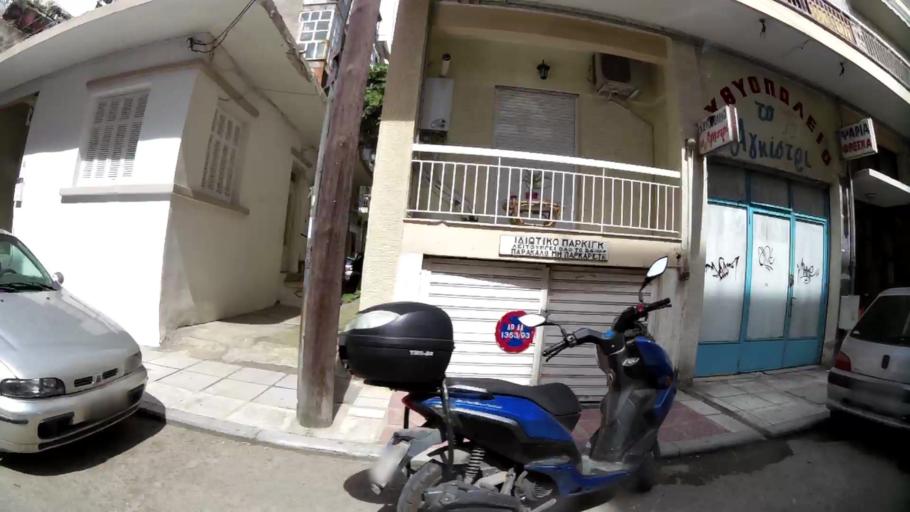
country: GR
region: Central Macedonia
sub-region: Nomos Thessalonikis
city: Triandria
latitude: 40.6062
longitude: 22.9617
